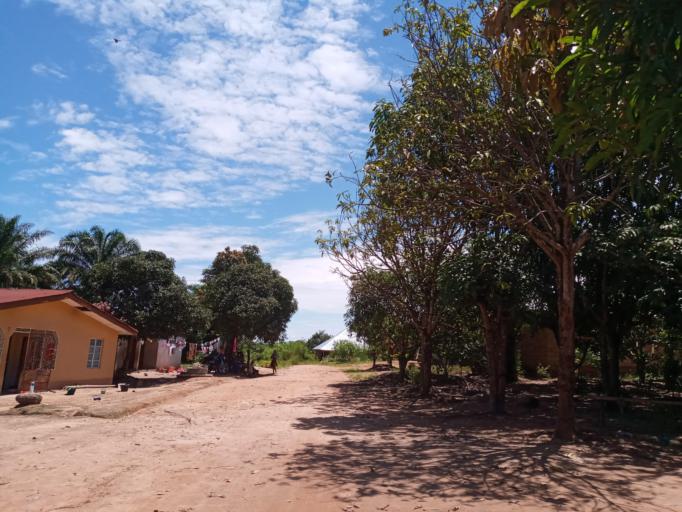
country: SL
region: Eastern Province
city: Koidu
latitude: 8.6515
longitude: -10.9522
